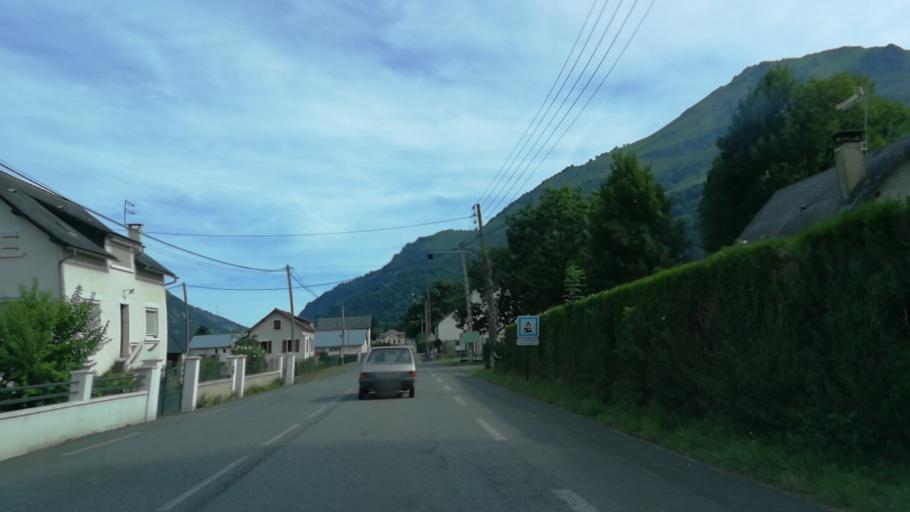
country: FR
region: Aquitaine
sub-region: Departement des Pyrenees-Atlantiques
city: Arette
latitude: 42.9916
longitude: -0.6028
